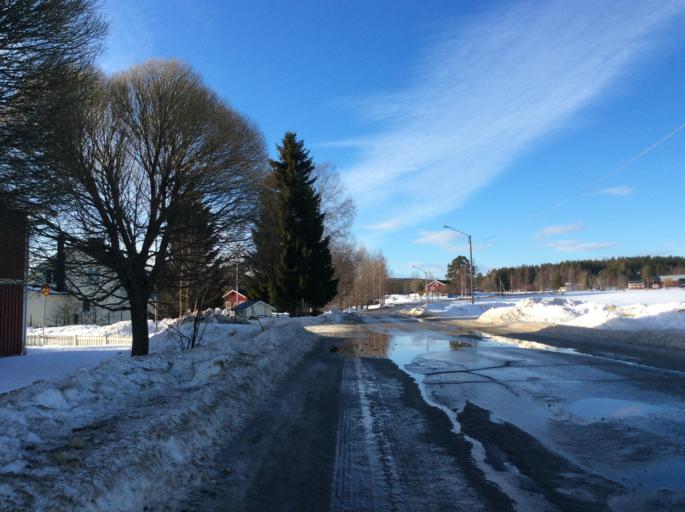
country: SE
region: Vaesterbotten
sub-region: Umea Kommun
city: Roback
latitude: 64.0387
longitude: 20.0751
